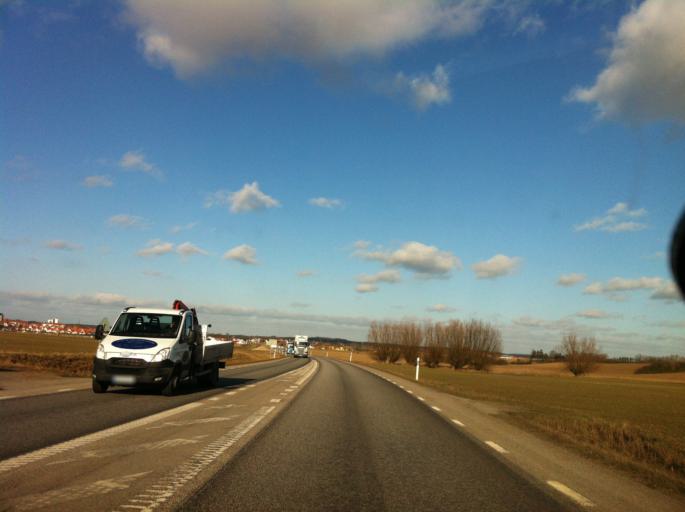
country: SE
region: Skane
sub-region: Svedala Kommun
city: Svedala
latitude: 55.4922
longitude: 13.2404
